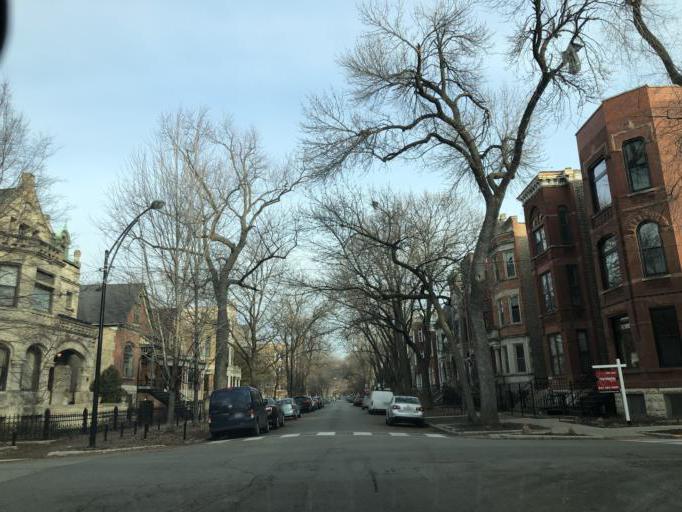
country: US
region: Illinois
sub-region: Cook County
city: Chicago
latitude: 41.9003
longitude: -87.6796
